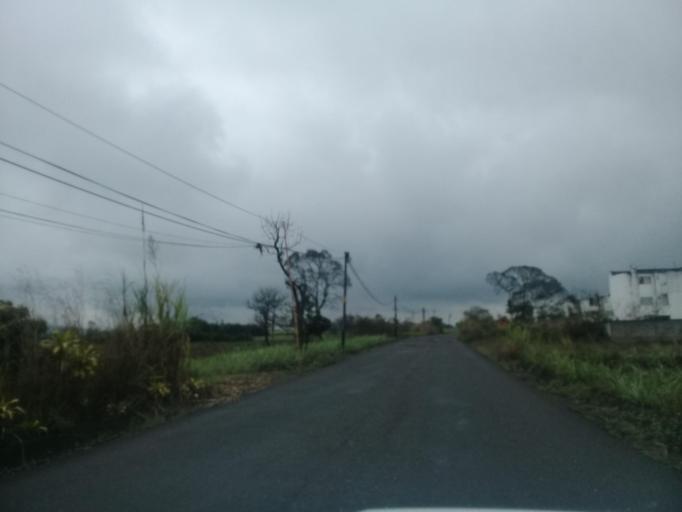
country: MX
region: Veracruz
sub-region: Cordoba
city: San Jose de Tapia
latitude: 18.8350
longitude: -96.9565
